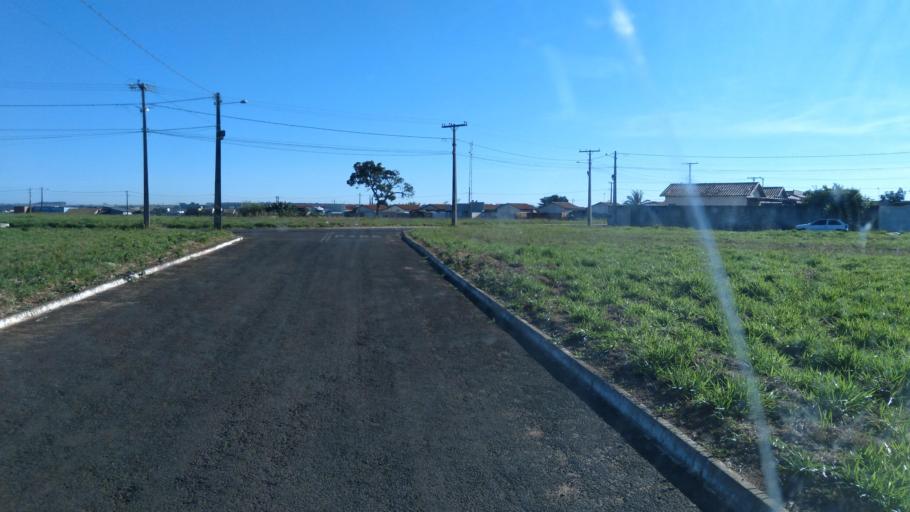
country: BR
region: Goias
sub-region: Mineiros
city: Mineiros
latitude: -17.5451
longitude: -52.5504
